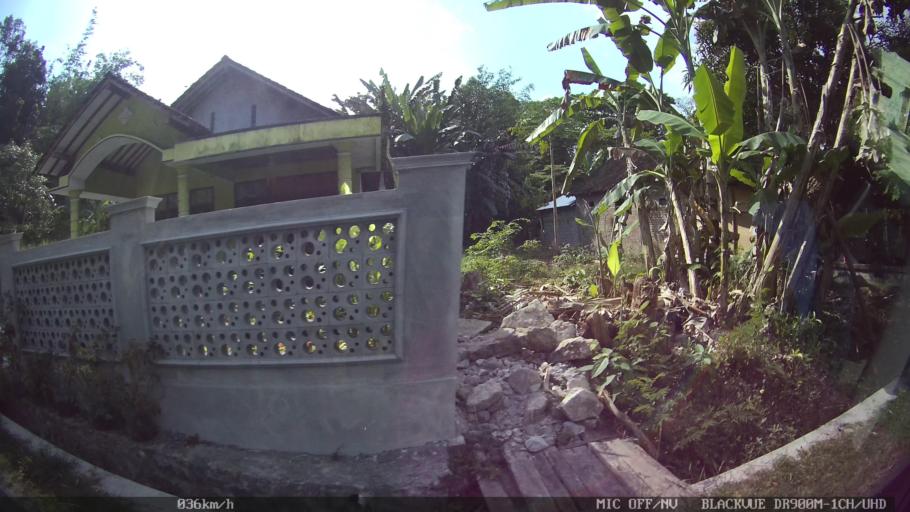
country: ID
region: Daerah Istimewa Yogyakarta
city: Kasihan
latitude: -7.8417
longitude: 110.3106
